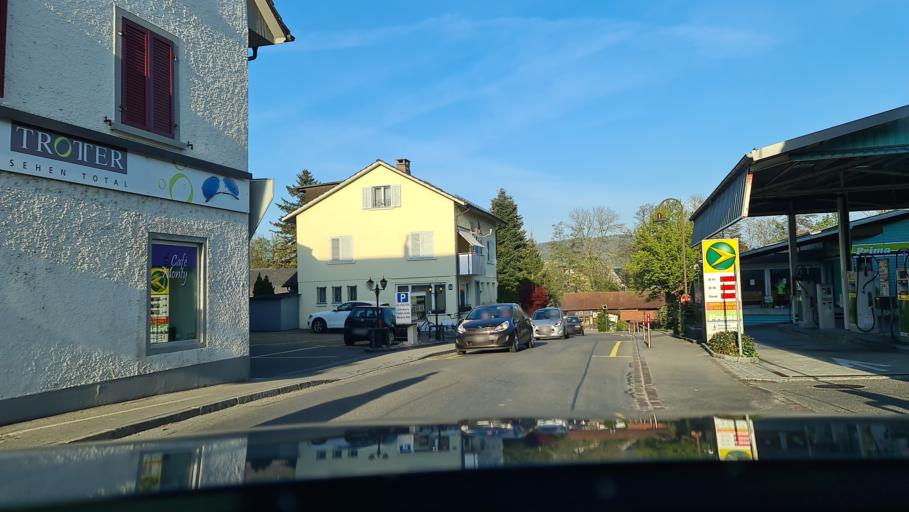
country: CH
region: Aargau
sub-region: Bezirk Lenzburg
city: Seon
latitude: 47.3454
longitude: 8.1603
